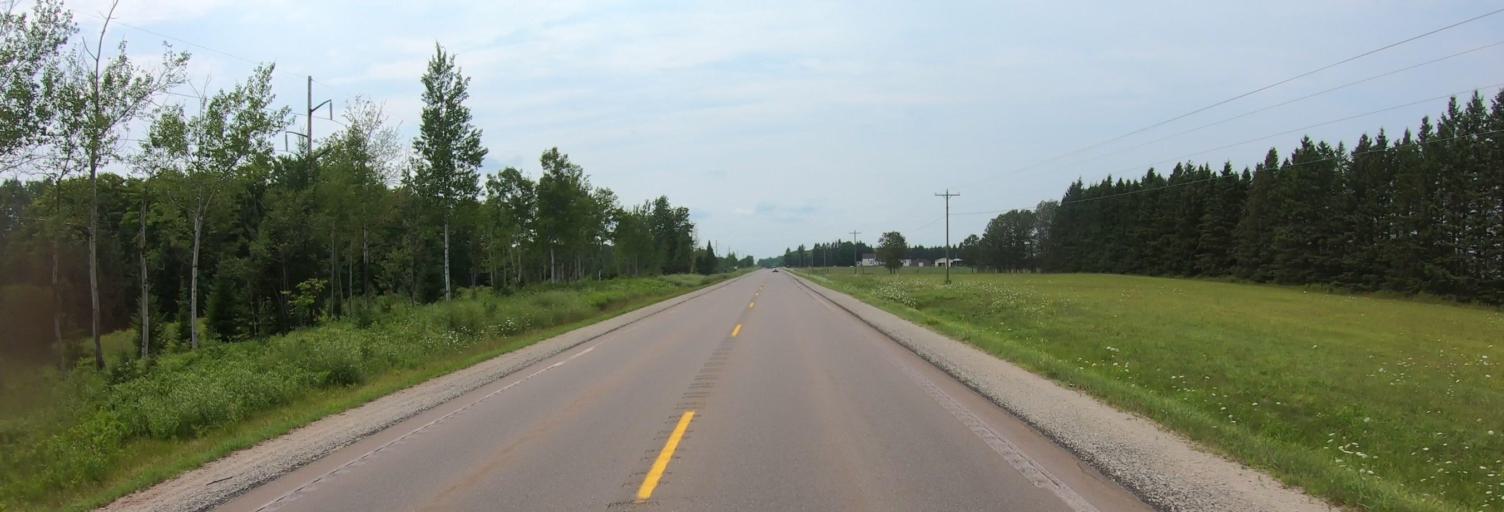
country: US
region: Michigan
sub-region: Marquette County
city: Harvey
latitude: 46.3507
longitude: -87.0212
